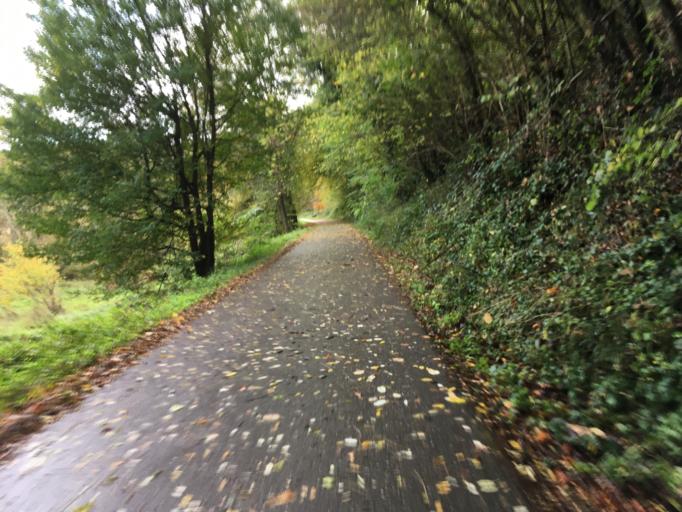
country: DE
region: Baden-Wuerttemberg
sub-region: Regierungsbezirk Stuttgart
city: Mockmuhl
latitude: 49.3135
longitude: 9.3790
